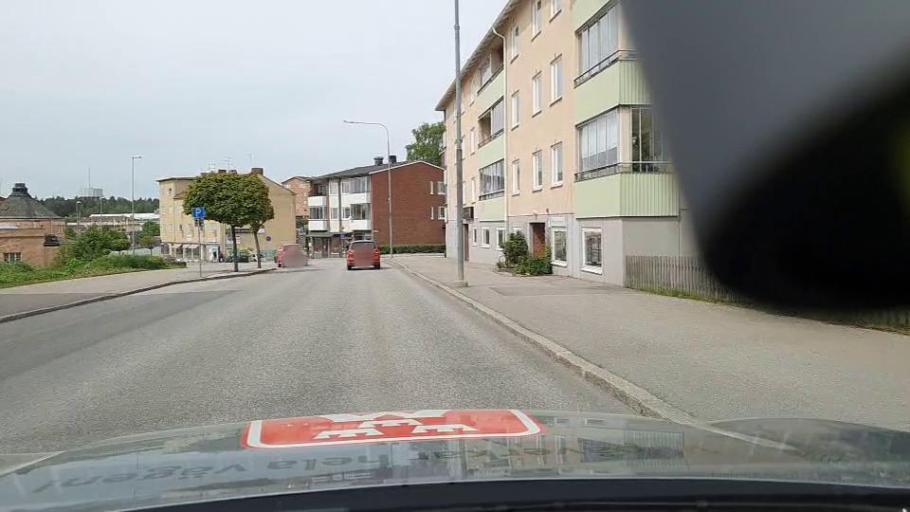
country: SE
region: Soedermanland
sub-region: Flens Kommun
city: Flen
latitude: 59.0572
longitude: 16.5945
